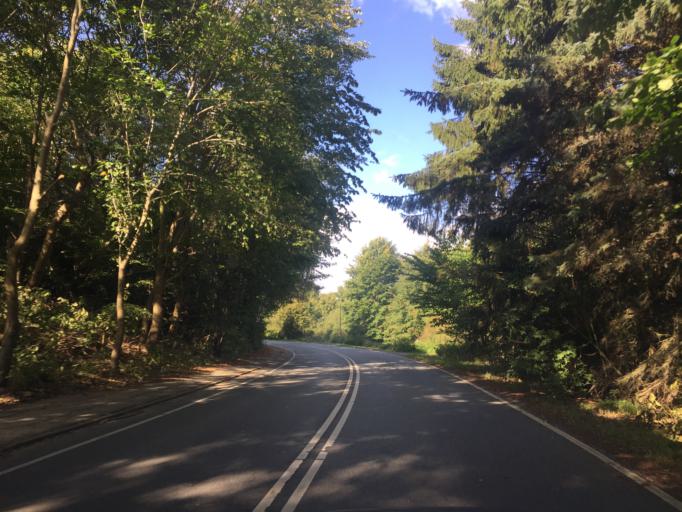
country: DK
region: Capital Region
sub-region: Gribskov Kommune
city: Helsinge
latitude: 56.0530
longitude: 12.1054
